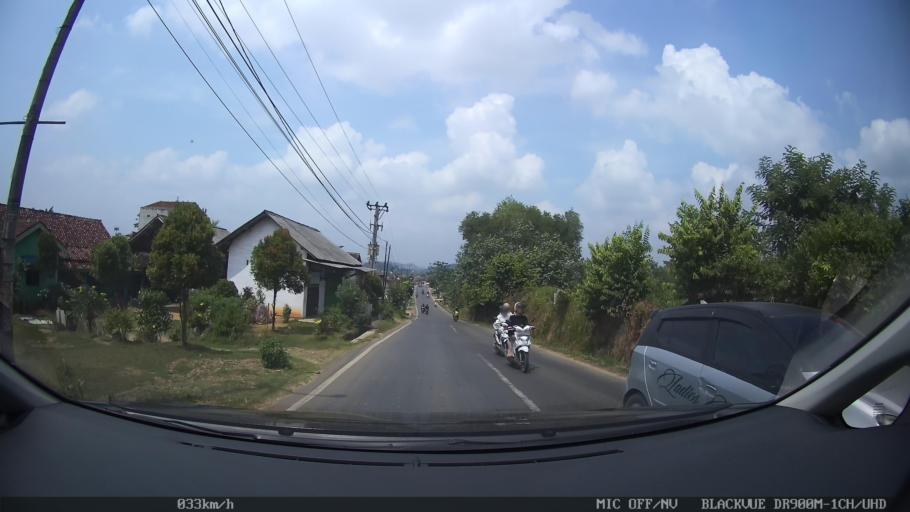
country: ID
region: Lampung
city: Pringsewu
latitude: -5.3677
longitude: 104.9684
